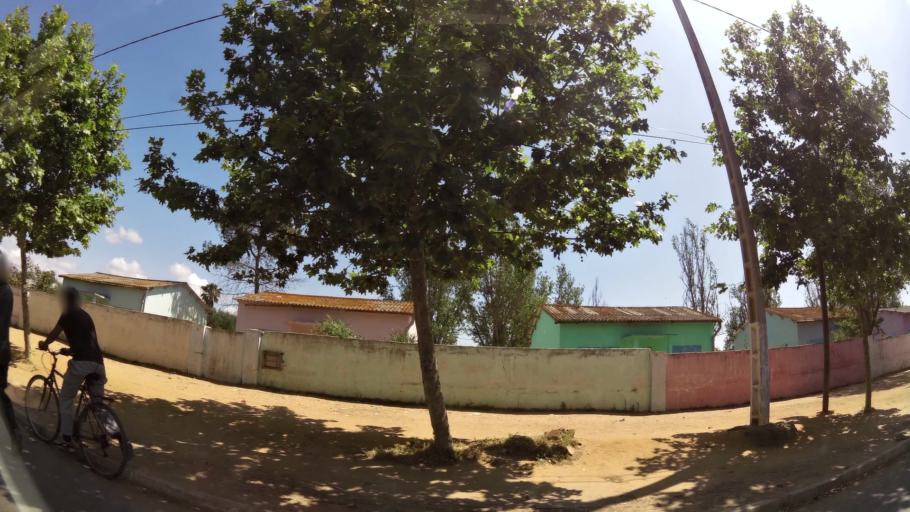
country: MA
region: Gharb-Chrarda-Beni Hssen
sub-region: Kenitra Province
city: Kenitra
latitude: 34.2327
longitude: -6.5371
